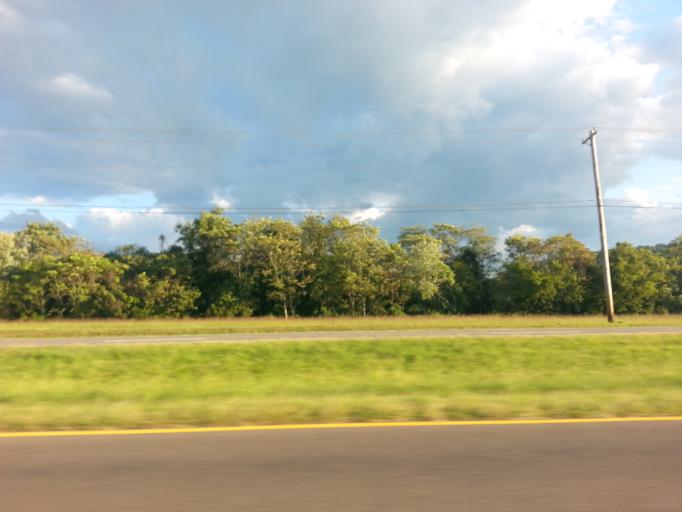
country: US
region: Tennessee
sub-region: Jefferson County
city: New Market
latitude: 36.1034
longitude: -83.5442
